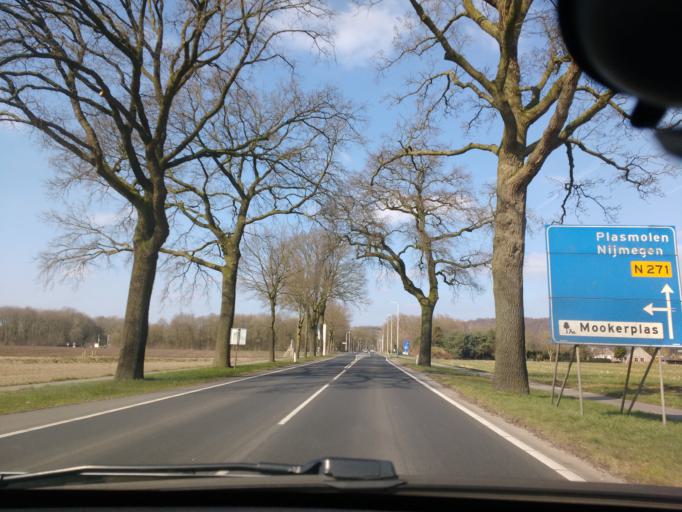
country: NL
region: Gelderland
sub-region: Gemeente Groesbeek
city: Bredeweg
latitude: 51.7313
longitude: 5.9367
